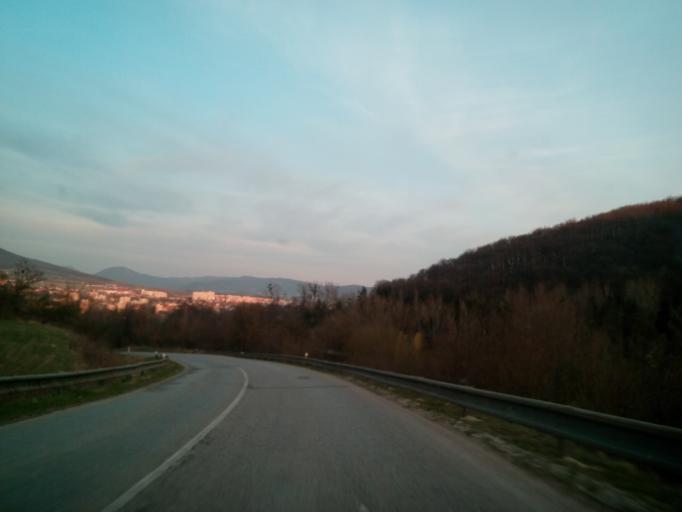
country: SK
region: Kosicky
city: Roznava
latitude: 48.6591
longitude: 20.5059
